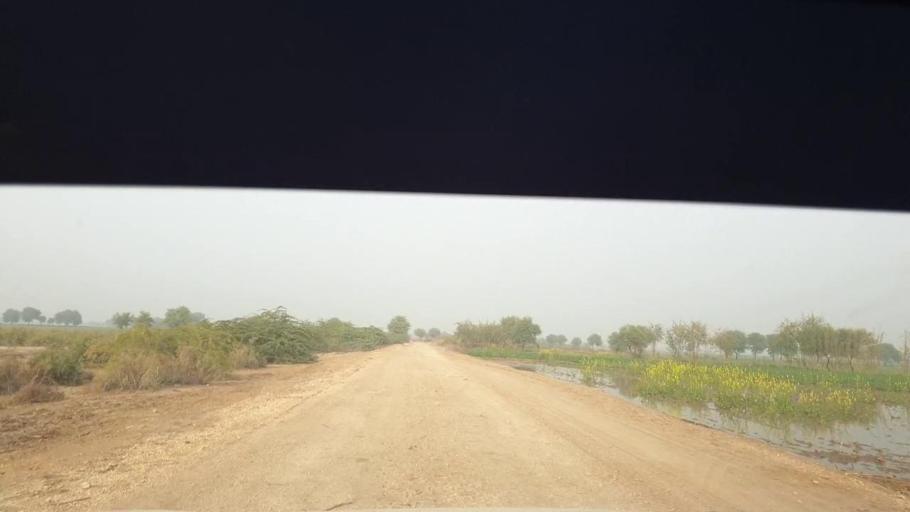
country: PK
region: Sindh
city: Berani
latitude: 25.8197
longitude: 68.8885
